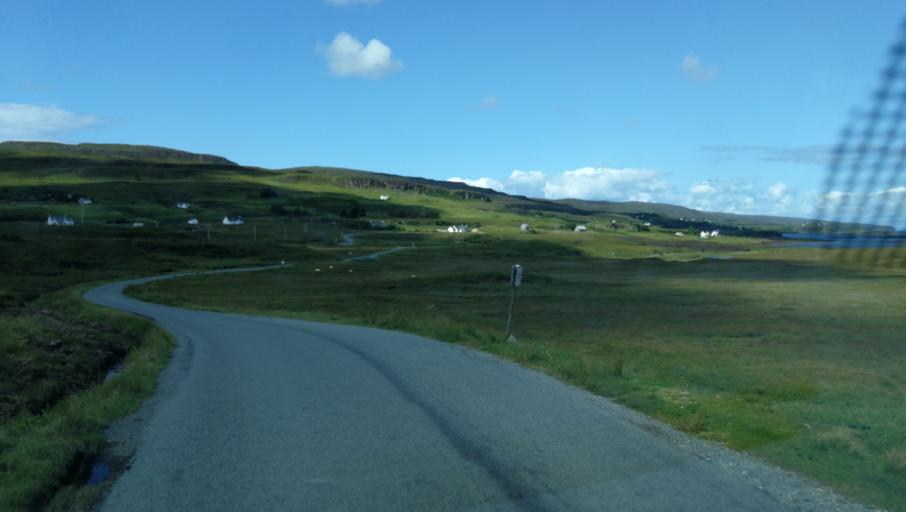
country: GB
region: Scotland
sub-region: Highland
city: Isle of Skye
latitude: 57.4297
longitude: -6.6154
